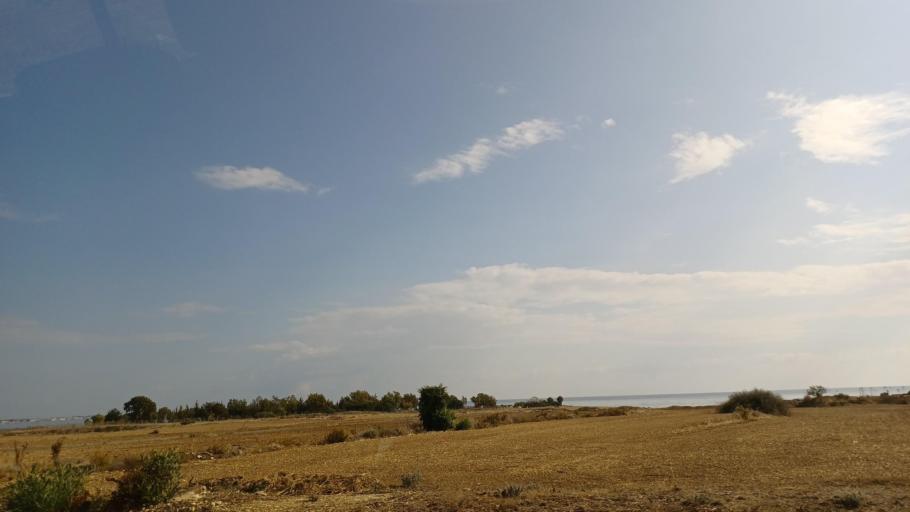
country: CY
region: Larnaka
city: Tersefanou
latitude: 34.8130
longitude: 33.5332
